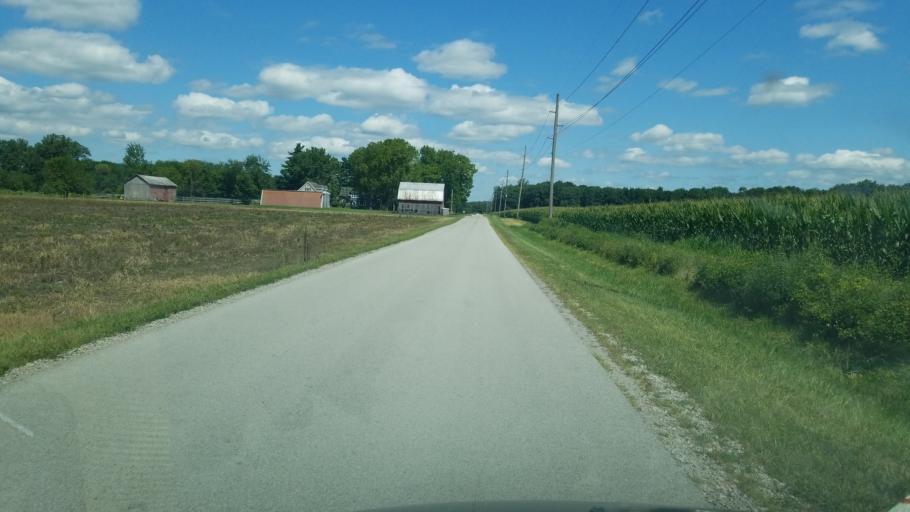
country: US
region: Ohio
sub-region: Wood County
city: Weston
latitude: 41.4235
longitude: -83.8653
